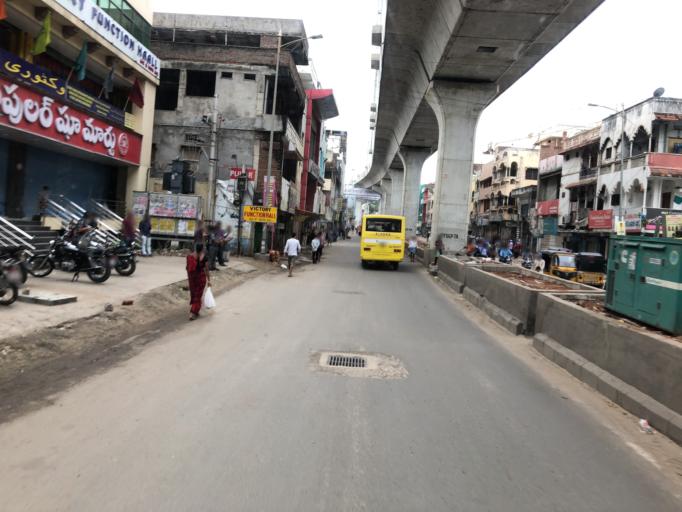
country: IN
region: Telangana
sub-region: Rangareddi
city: Kukatpalli
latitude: 17.4334
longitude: 78.4267
